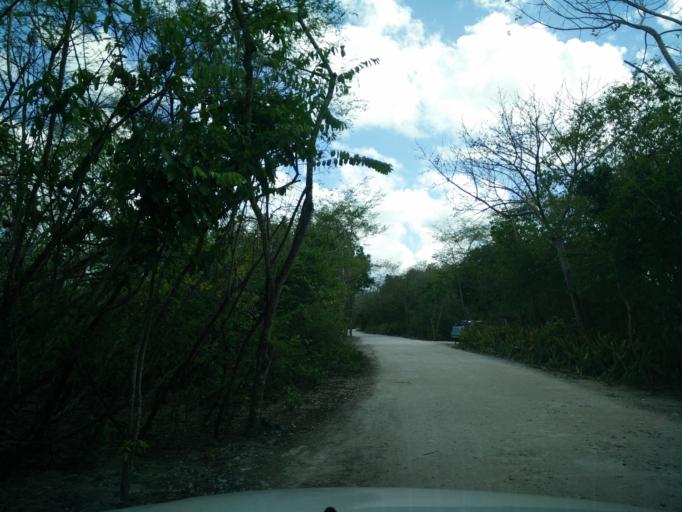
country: GP
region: Guadeloupe
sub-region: Guadeloupe
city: Port-Louis
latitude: 16.4360
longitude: -61.5368
